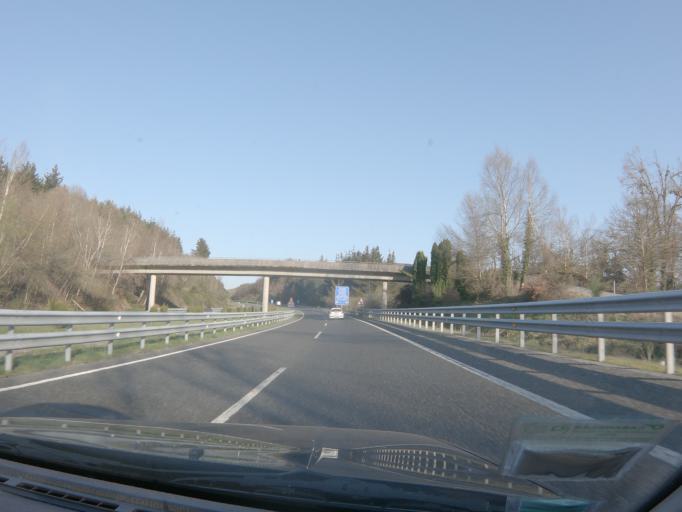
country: ES
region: Galicia
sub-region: Provincia de Lugo
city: Lancara
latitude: 42.9107
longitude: -7.3298
